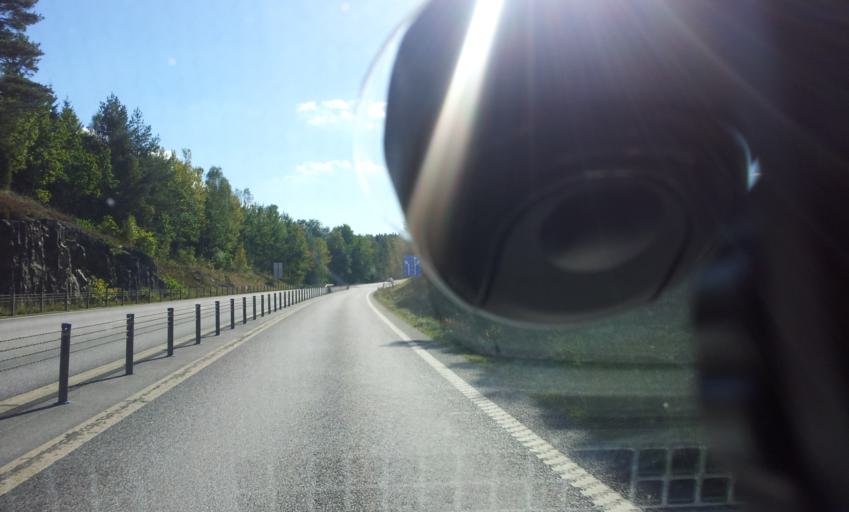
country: SE
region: OEstergoetland
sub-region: Valdemarsviks Kommun
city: Valdemarsvik
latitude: 58.1132
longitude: 16.5424
